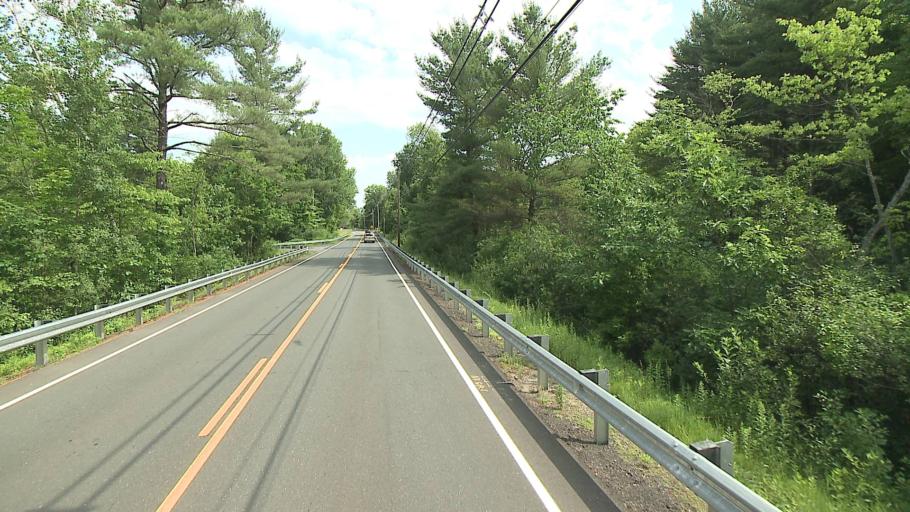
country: US
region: Connecticut
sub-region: Litchfield County
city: Winsted
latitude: 41.8840
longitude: -73.0751
